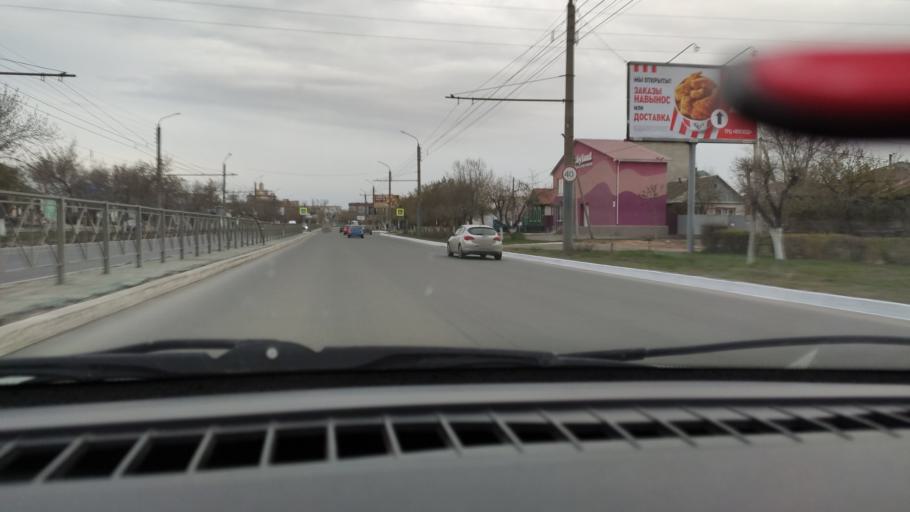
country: RU
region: Orenburg
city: Orenburg
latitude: 51.7874
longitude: 55.1066
